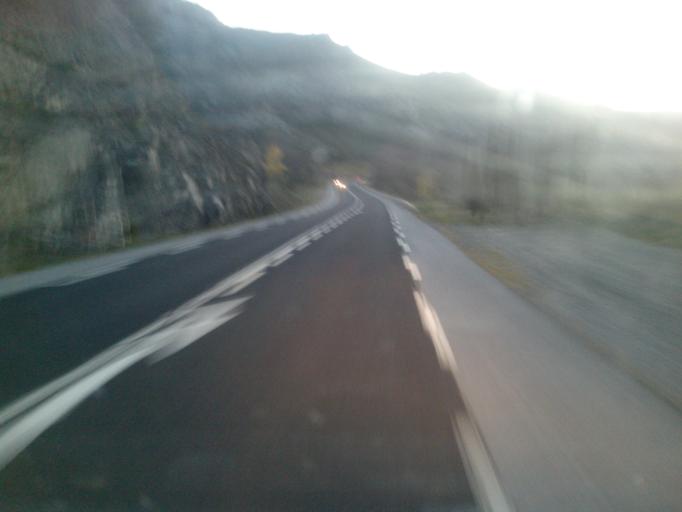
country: FR
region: Languedoc-Roussillon
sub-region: Departement des Pyrenees-Orientales
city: Baixas
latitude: 42.7756
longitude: 2.7676
